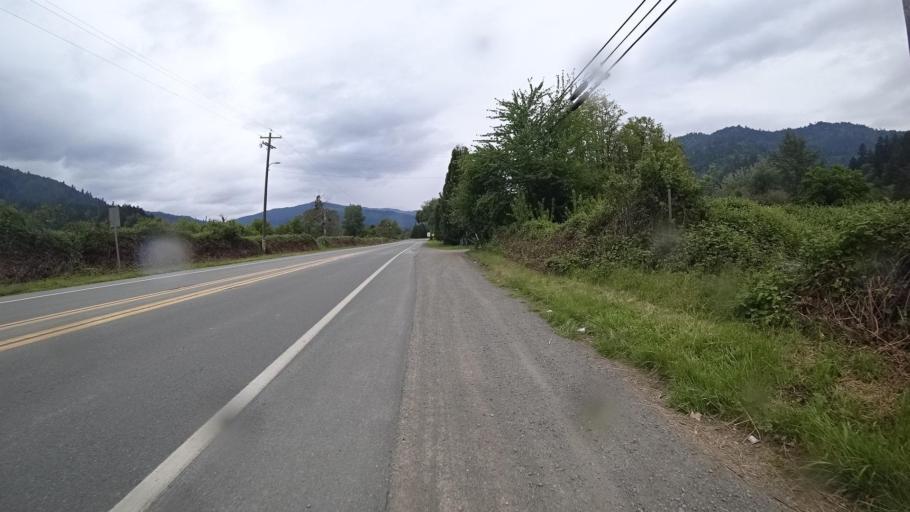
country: US
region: California
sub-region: Humboldt County
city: Willow Creek
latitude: 41.0702
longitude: -123.6871
